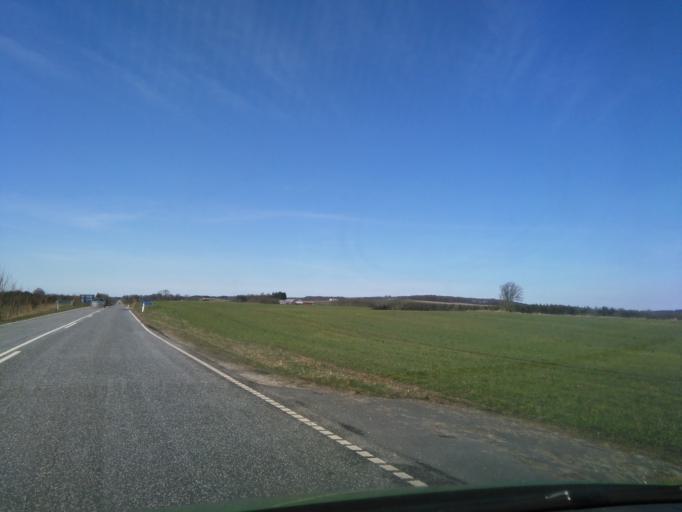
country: DK
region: Central Jutland
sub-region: Horsens Kommune
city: Braedstrup
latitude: 56.0214
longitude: 9.6084
